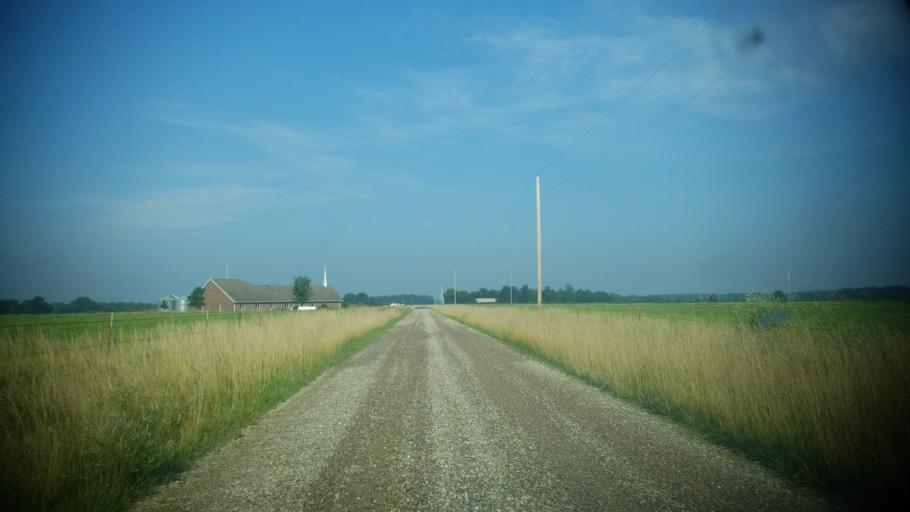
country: US
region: Illinois
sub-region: Clay County
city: Flora
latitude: 38.6024
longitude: -88.3798
